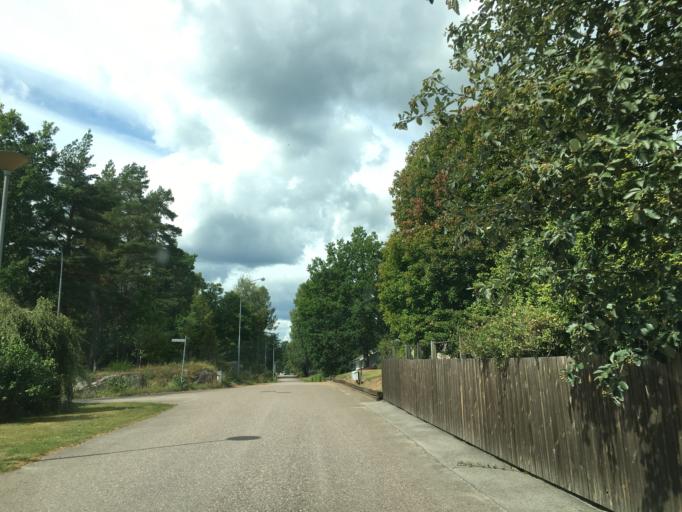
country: SE
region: Kalmar
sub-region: Nybro Kommun
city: Nybro
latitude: 56.9409
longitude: 15.9198
